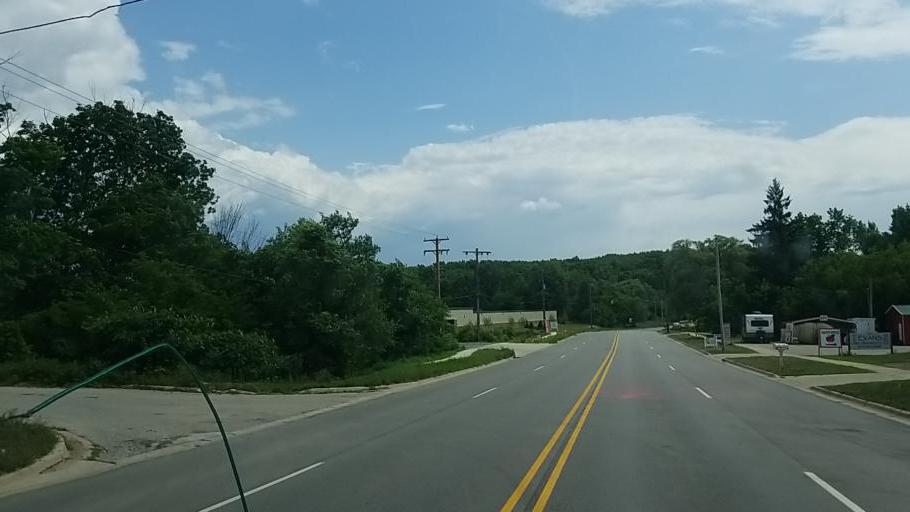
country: US
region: Michigan
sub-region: Kent County
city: Walker
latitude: 43.0027
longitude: -85.7191
